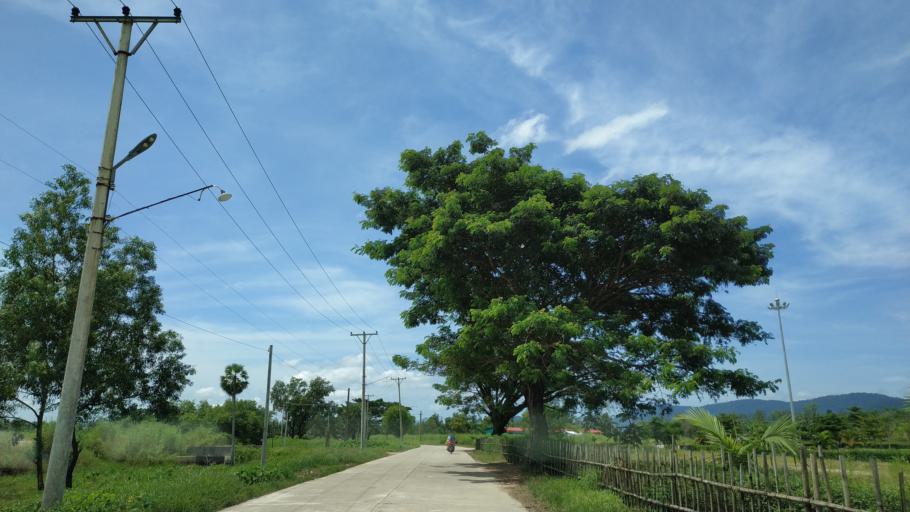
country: MM
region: Tanintharyi
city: Dawei
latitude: 14.0931
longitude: 98.1777
